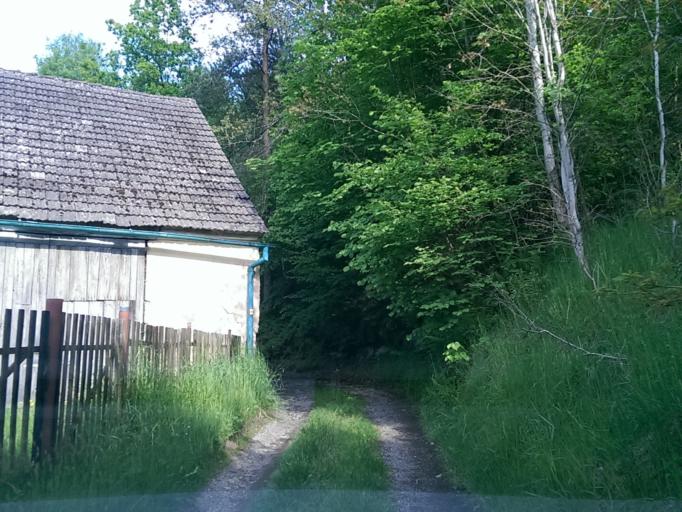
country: CZ
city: Duba
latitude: 50.5241
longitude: 14.5214
